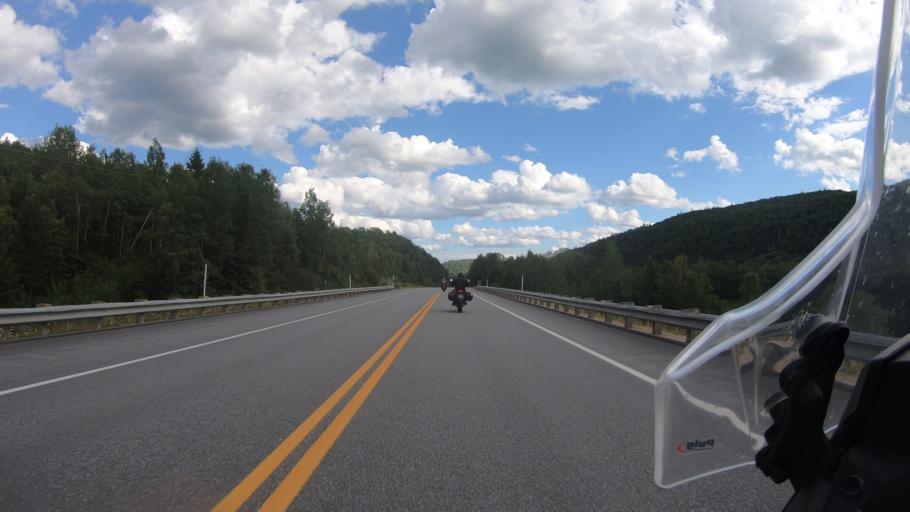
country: CA
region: Quebec
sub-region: Mauricie
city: Saint-Tite
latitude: 47.0048
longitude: -72.9265
